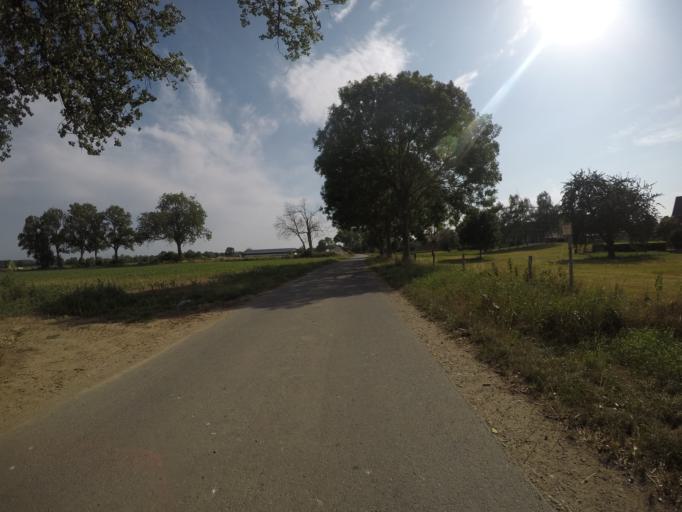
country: DE
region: North Rhine-Westphalia
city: Kalkar
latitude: 51.7457
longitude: 6.3359
